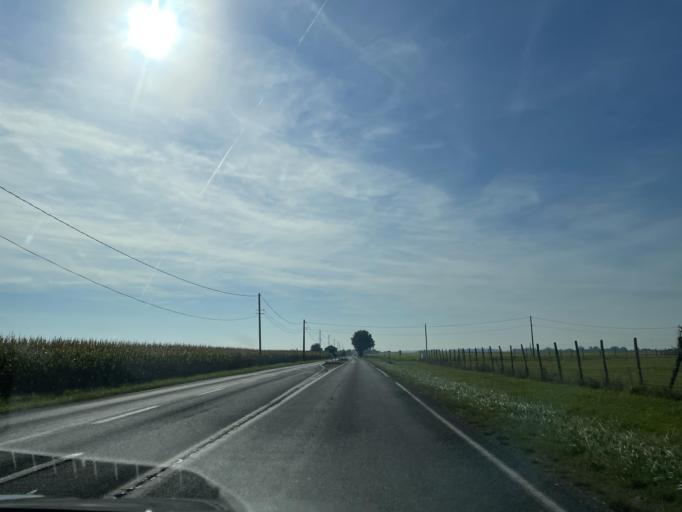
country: FR
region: Ile-de-France
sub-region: Departement de Seine-et-Marne
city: Coulommiers
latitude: 48.8684
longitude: 3.0917
